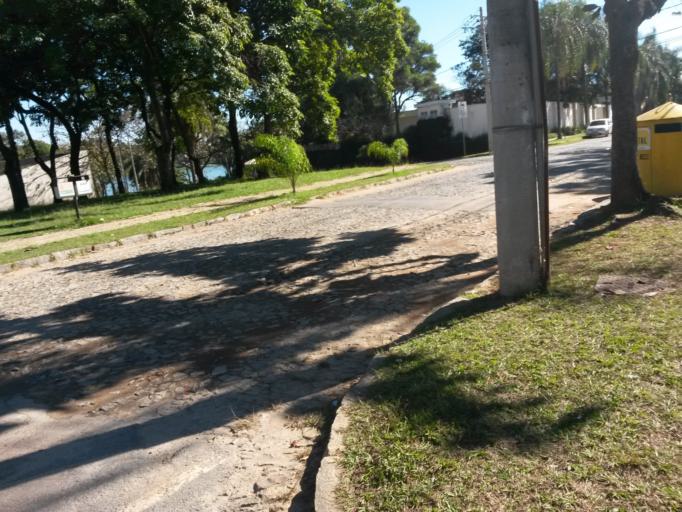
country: BR
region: Minas Gerais
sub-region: Belo Horizonte
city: Belo Horizonte
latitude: -19.8539
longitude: -43.9671
